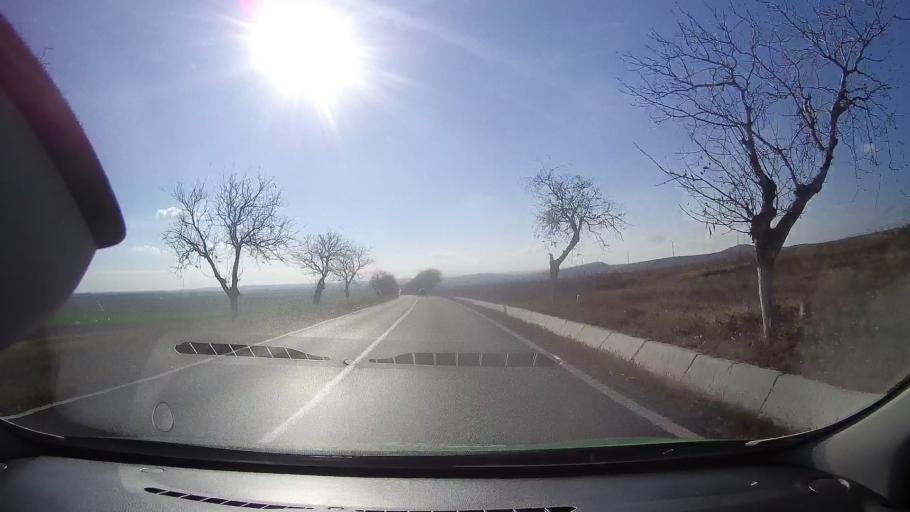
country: RO
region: Tulcea
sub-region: Comuna Ceamurlia de Jos
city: Ceamurlia de Jos
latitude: 44.8068
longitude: 28.6910
